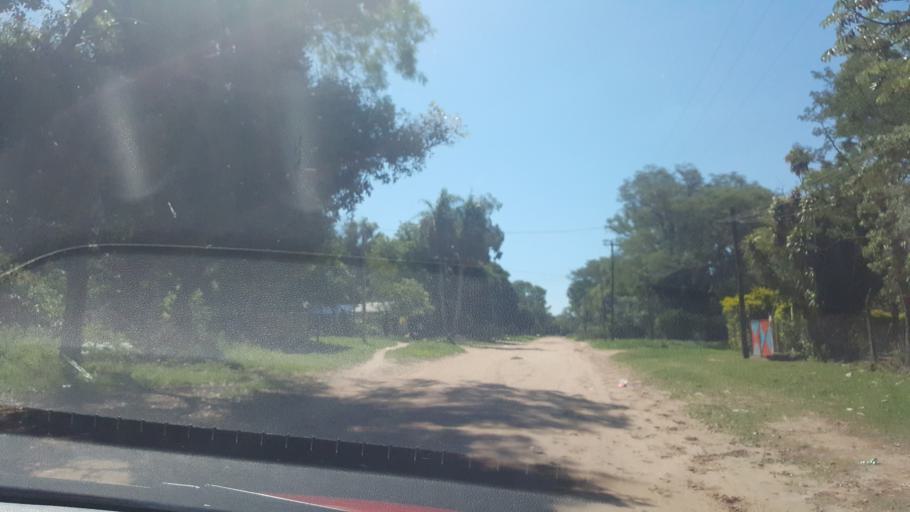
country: AR
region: Corrientes
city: Ituzaingo
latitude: -27.5956
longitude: -56.7059
